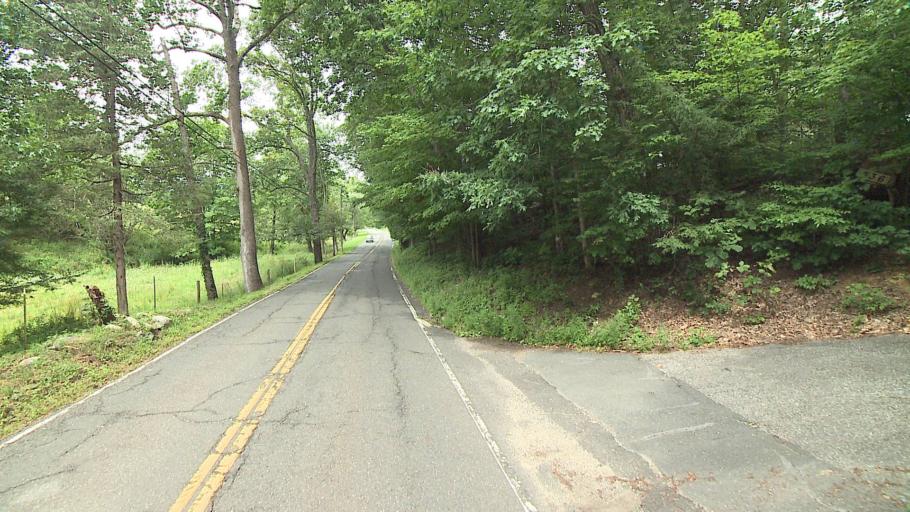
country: US
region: Connecticut
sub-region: Litchfield County
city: New Milford
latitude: 41.5073
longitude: -73.3598
